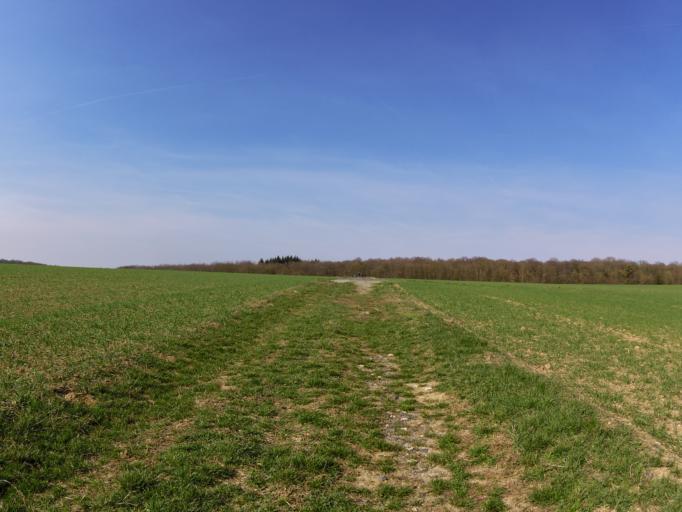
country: DE
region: Bavaria
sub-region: Regierungsbezirk Unterfranken
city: Rottendorf
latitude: 49.8057
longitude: 10.0375
